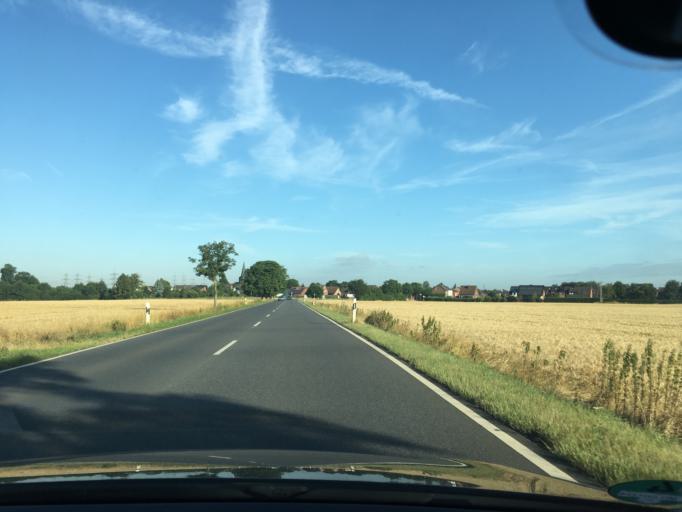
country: DE
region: North Rhine-Westphalia
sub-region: Regierungsbezirk Koln
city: Niederzier
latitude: 50.8633
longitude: 6.4806
